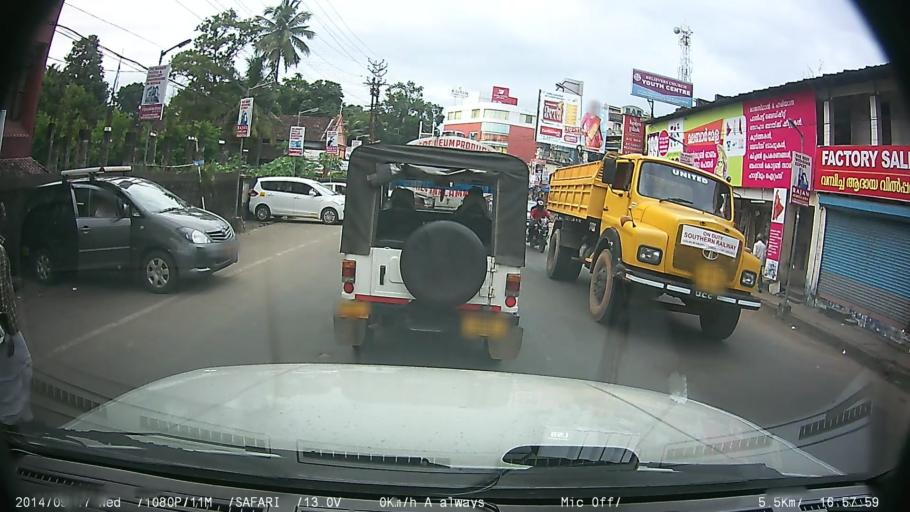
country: IN
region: Kerala
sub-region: Pattanamtitta
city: Tiruvalla
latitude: 9.3875
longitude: 76.5751
